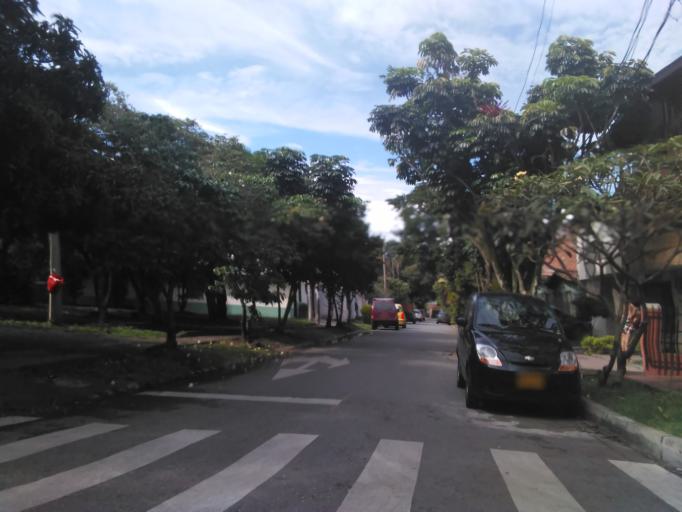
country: CO
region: Antioquia
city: Medellin
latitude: 6.2354
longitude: -75.5850
